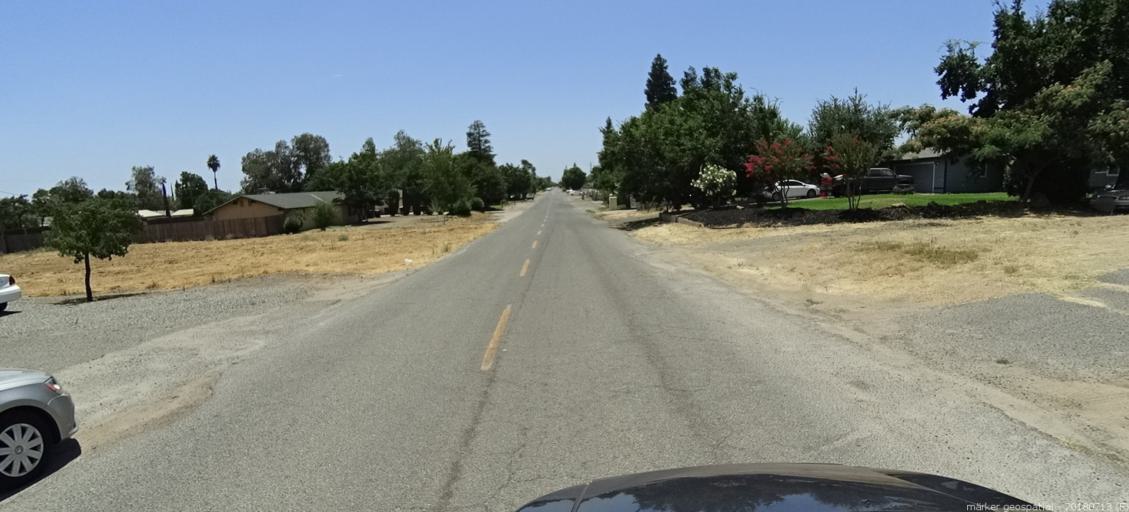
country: US
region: California
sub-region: Madera County
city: Madera Acres
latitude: 36.9986
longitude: -120.0805
